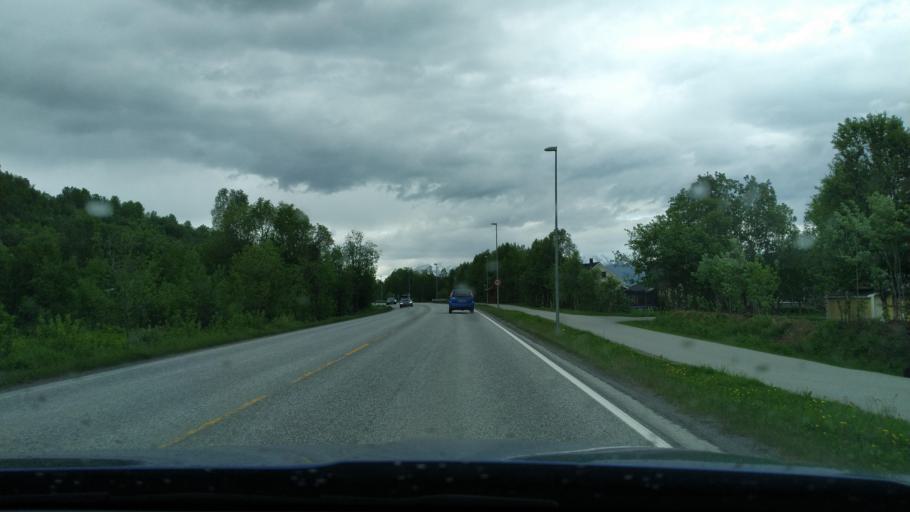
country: NO
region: Troms
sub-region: Malselv
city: Moen
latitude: 69.0330
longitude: 18.5046
